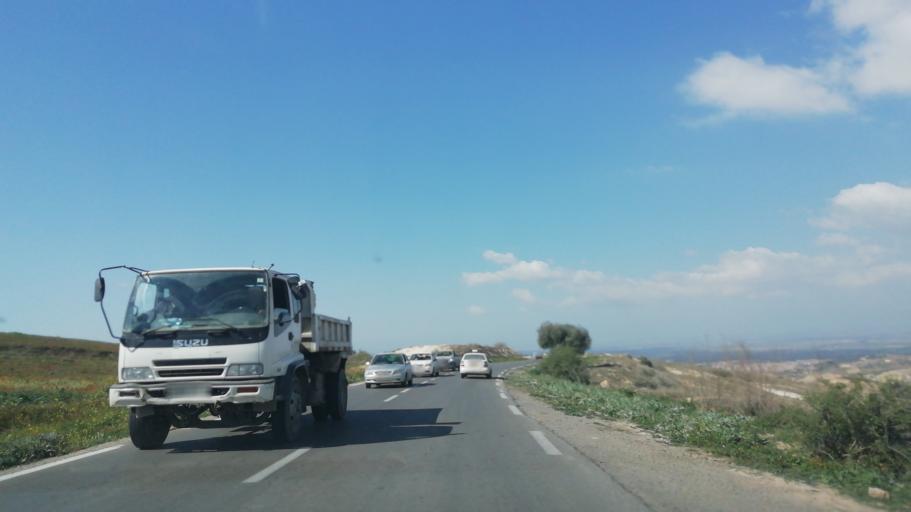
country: DZ
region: Mascara
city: Mascara
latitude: 35.5433
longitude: 0.0911
